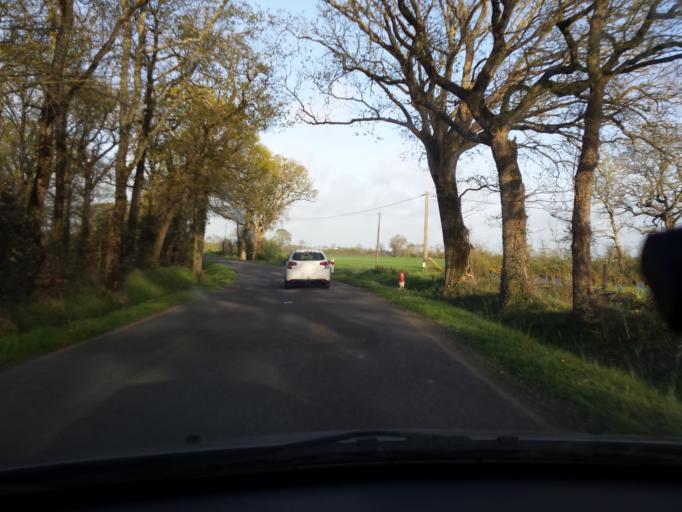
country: FR
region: Pays de la Loire
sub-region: Departement de la Vendee
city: Vaire
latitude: 46.5691
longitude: -1.7523
